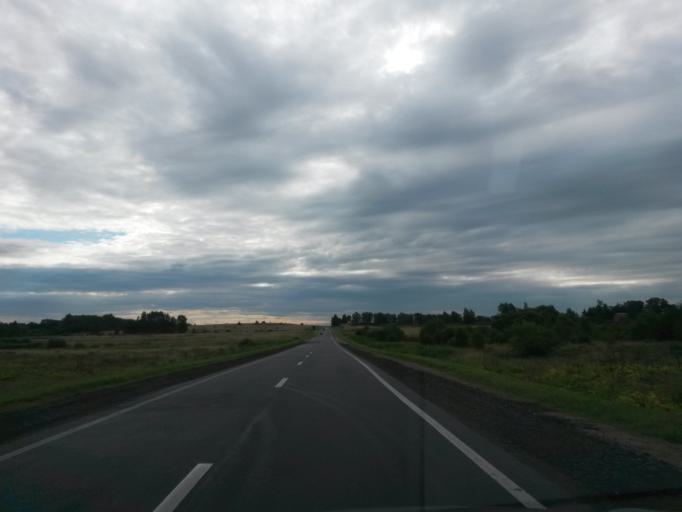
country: RU
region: Jaroslavl
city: Gavrilov-Yam
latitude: 57.3603
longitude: 39.7621
